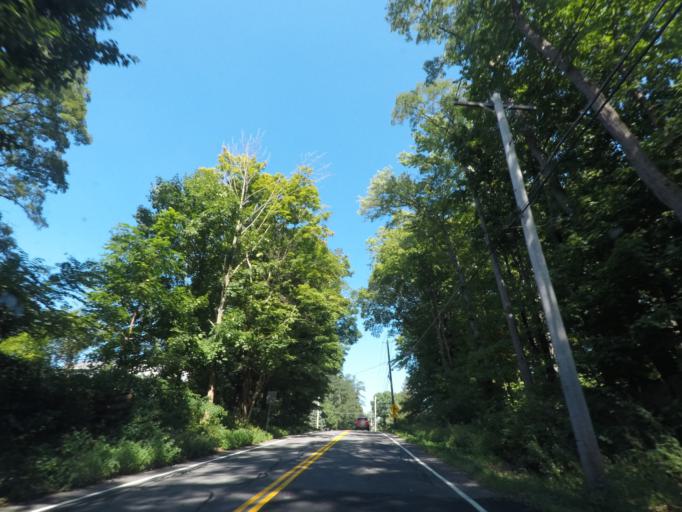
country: US
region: New York
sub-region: Schenectady County
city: Niskayuna
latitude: 42.7673
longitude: -73.7877
